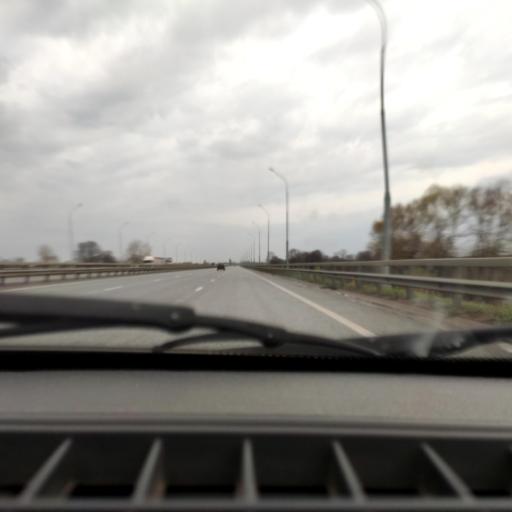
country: RU
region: Bashkortostan
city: Ufa
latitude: 54.6448
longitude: 55.9789
